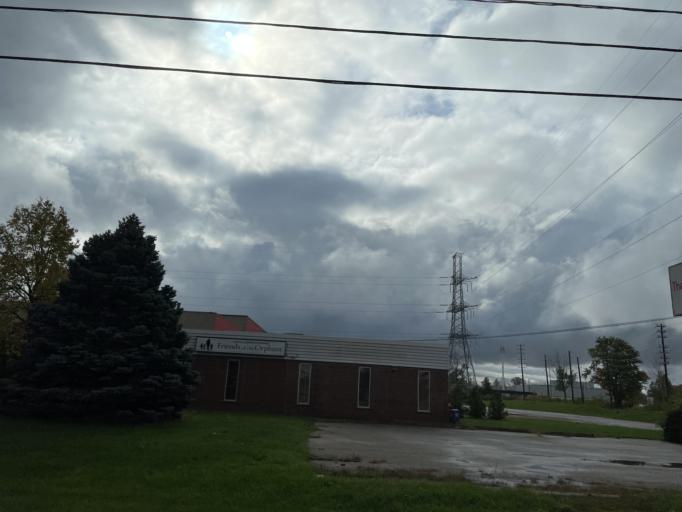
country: CA
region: Ontario
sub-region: Wellington County
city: Guelph
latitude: 43.5479
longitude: -80.2915
